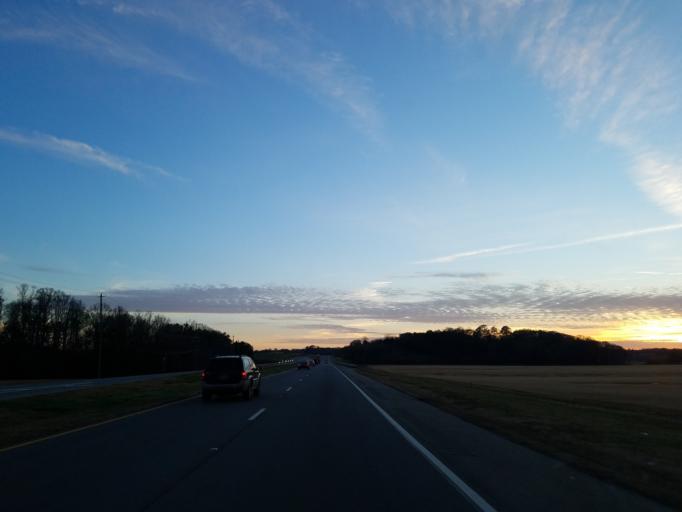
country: US
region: Georgia
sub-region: Bartow County
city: Cartersville
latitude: 34.1369
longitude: -84.8456
